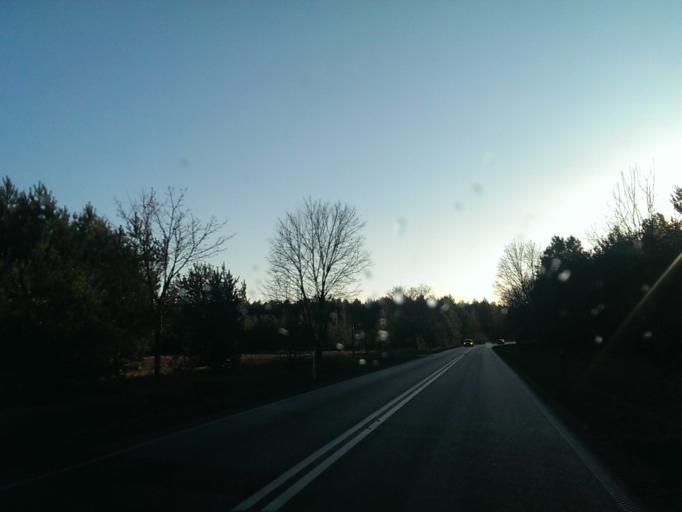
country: PL
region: Kujawsko-Pomorskie
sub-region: Powiat nakielski
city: Naklo nad Notecia
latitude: 53.0771
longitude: 17.5850
